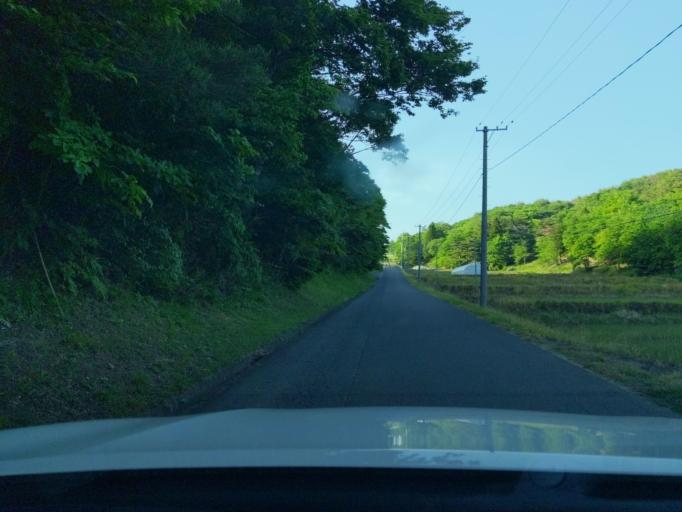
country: JP
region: Fukushima
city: Motomiya
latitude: 37.5231
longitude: 140.3324
